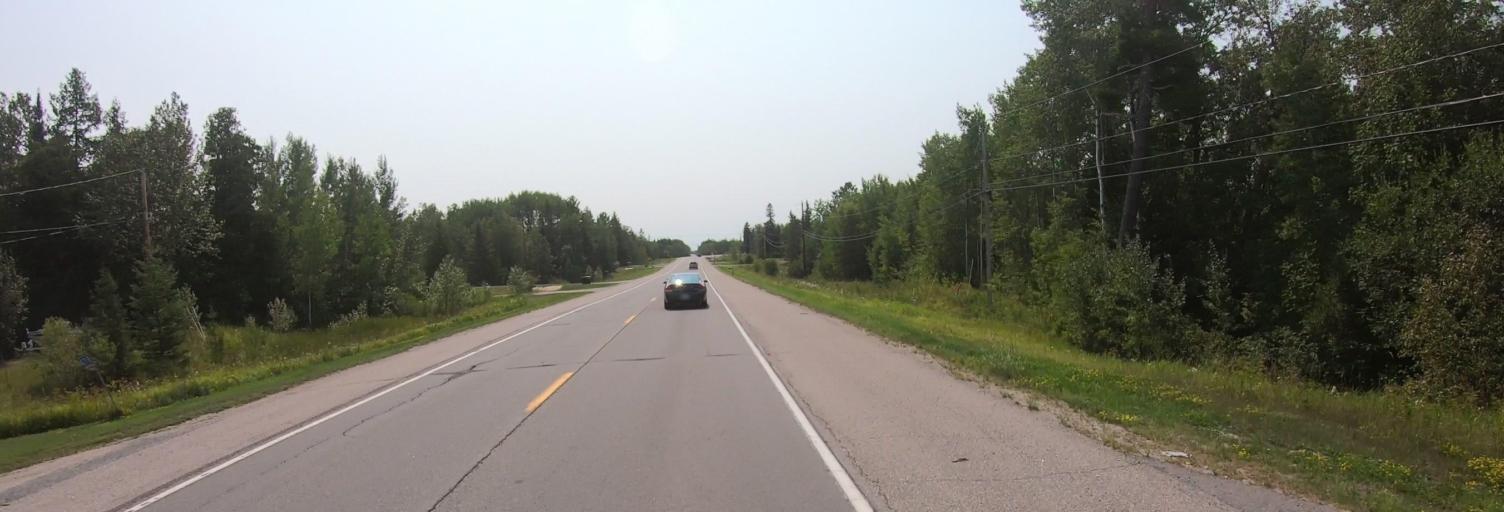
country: US
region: Minnesota
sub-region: Koochiching County
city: International Falls
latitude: 48.5614
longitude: -93.4401
